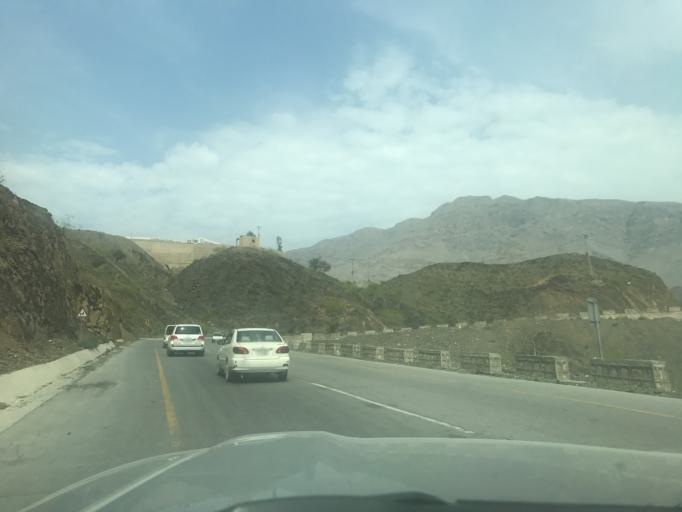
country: PK
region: Federally Administered Tribal Areas
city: Landi Kotal
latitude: 34.0072
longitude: 71.2990
